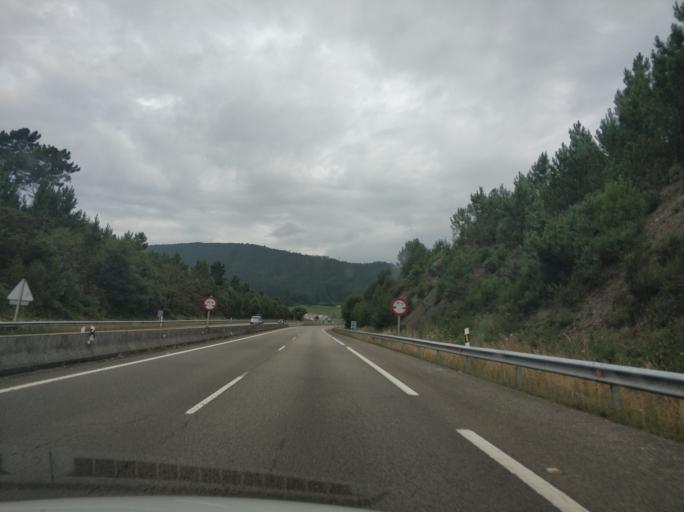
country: ES
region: Asturias
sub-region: Province of Asturias
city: Navia
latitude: 43.5328
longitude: -6.7366
